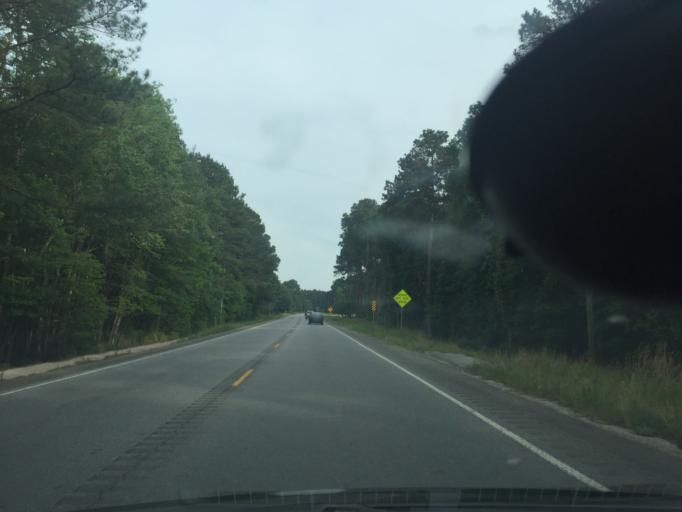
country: US
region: Georgia
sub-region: Bryan County
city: Richmond Hill
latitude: 32.0203
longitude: -81.3135
